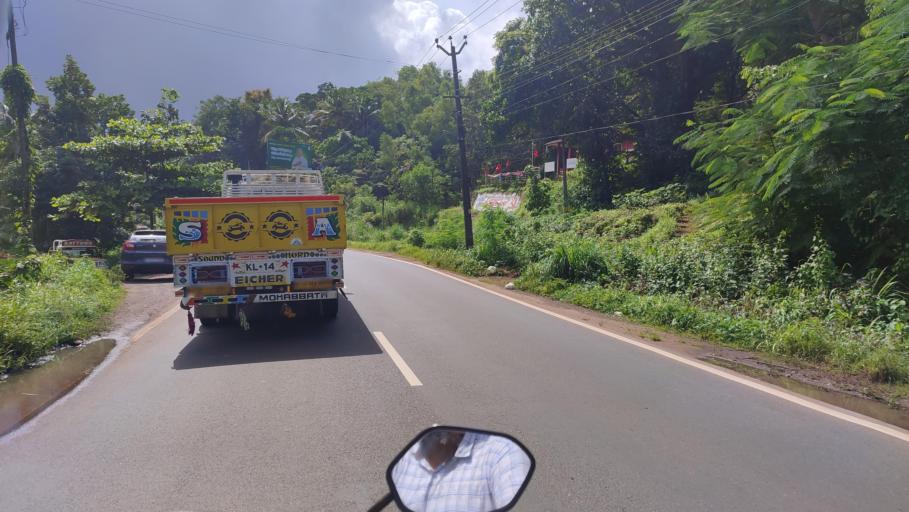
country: IN
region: Kerala
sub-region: Kasaragod District
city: Nileshwar
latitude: 12.2203
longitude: 75.1605
